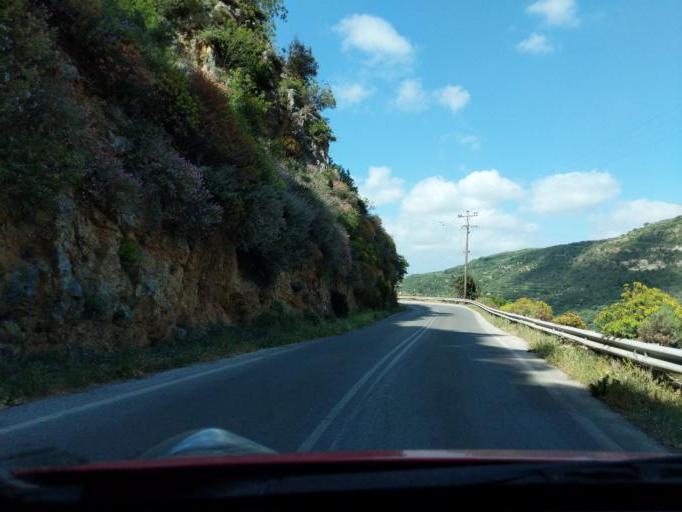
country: GR
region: Crete
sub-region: Nomos Chanias
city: Kissamos
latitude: 35.4213
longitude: 23.6884
